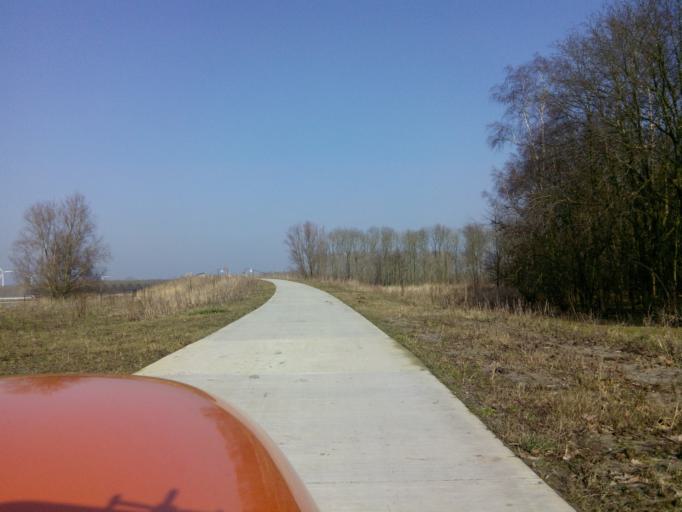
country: NL
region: Flevoland
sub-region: Gemeente Zeewolde
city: Zeewolde
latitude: 52.3232
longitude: 5.4487
